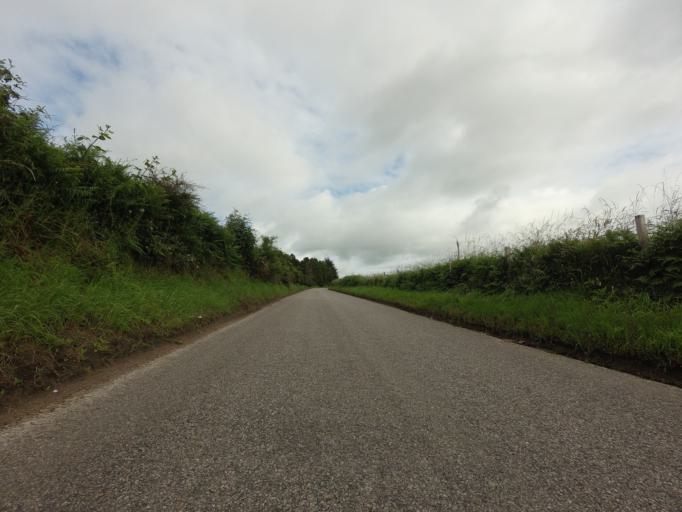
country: GB
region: Scotland
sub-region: Moray
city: Elgin
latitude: 57.6584
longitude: -3.3533
